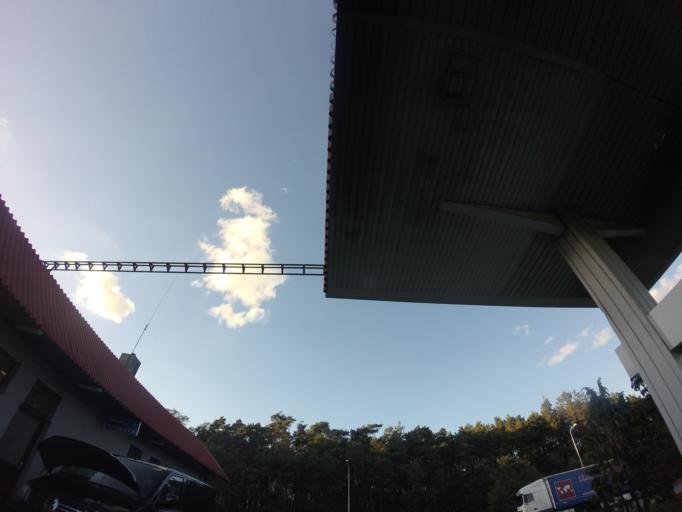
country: PL
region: Greater Poland Voivodeship
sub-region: Powiat nowotomyski
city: Miedzichowo
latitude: 52.3764
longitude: 15.9596
